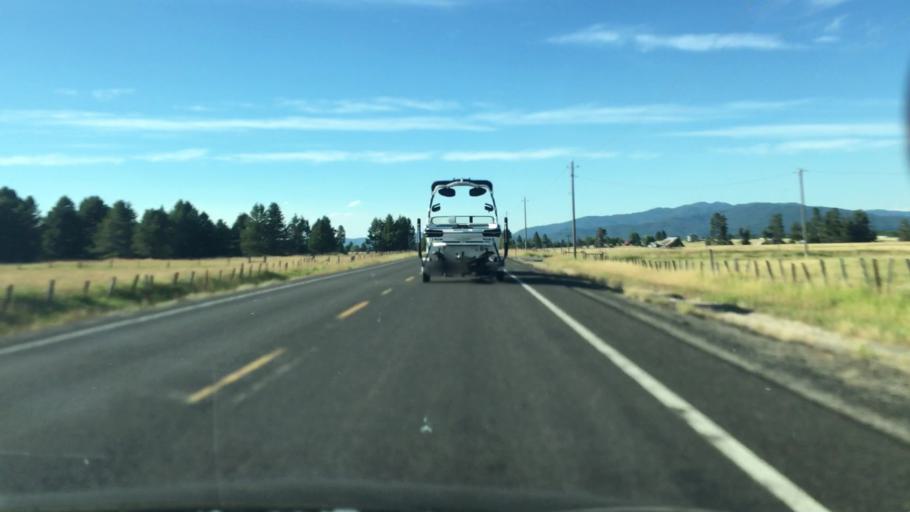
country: US
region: Idaho
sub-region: Valley County
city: Cascade
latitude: 44.4458
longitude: -115.9994
